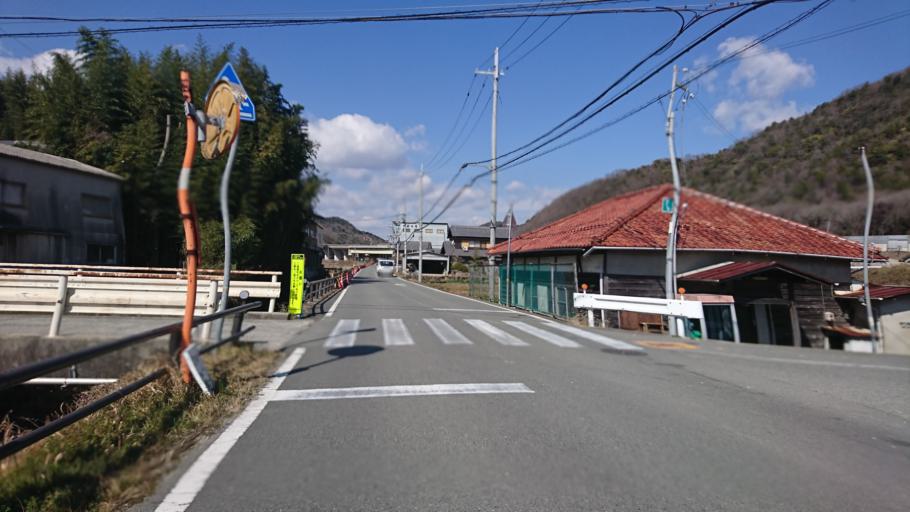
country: JP
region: Hyogo
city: Kakogawacho-honmachi
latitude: 34.8461
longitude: 134.8140
